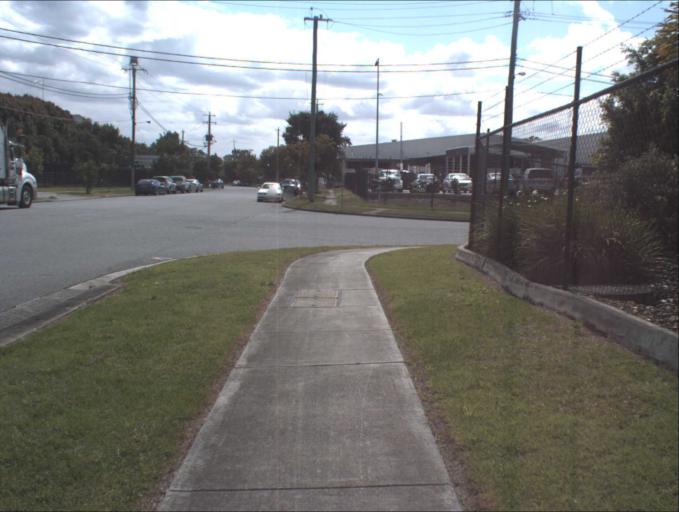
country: AU
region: Queensland
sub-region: Logan
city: Logan Reserve
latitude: -27.6836
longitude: 153.0761
